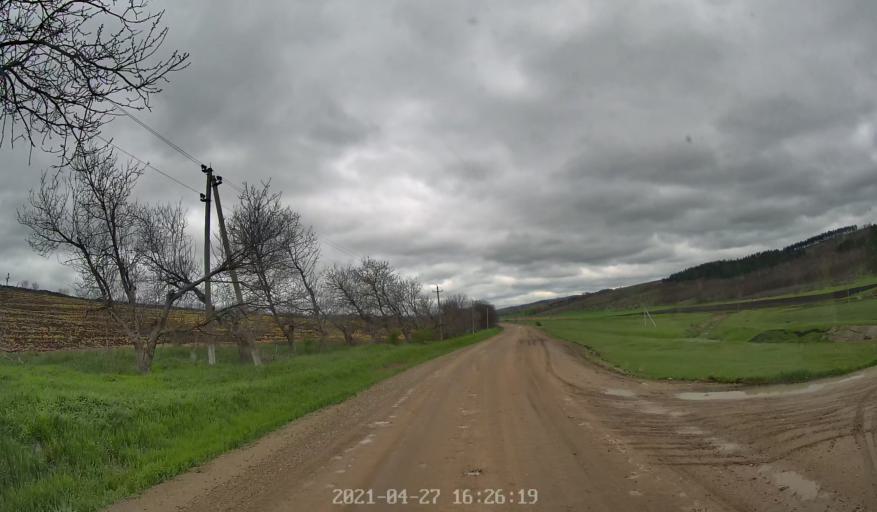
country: MD
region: Chisinau
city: Singera
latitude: 46.9804
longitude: 29.0253
